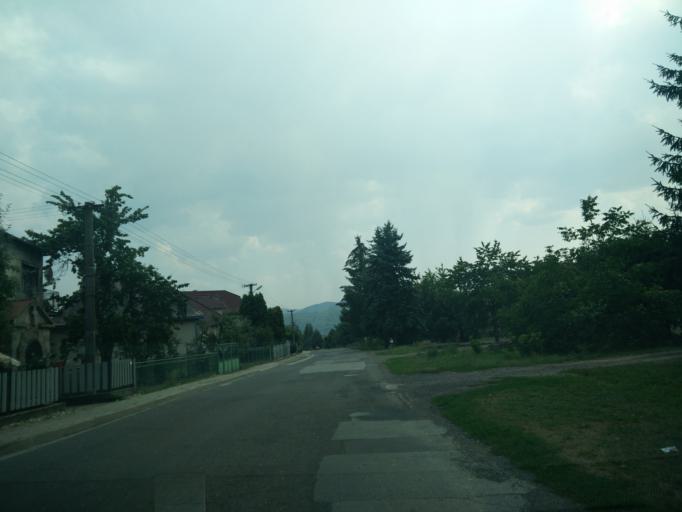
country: SK
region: Banskobystricky
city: Zarnovica
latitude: 48.5507
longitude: 18.7594
